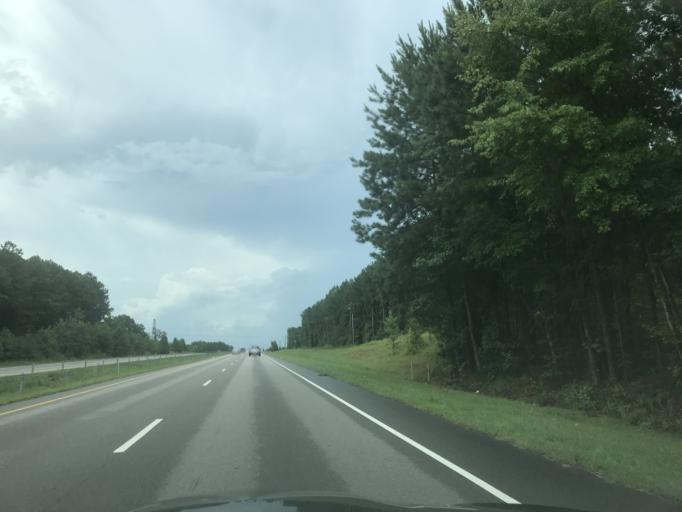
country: US
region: North Carolina
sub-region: Johnston County
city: Clayton
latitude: 35.6785
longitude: -78.5262
